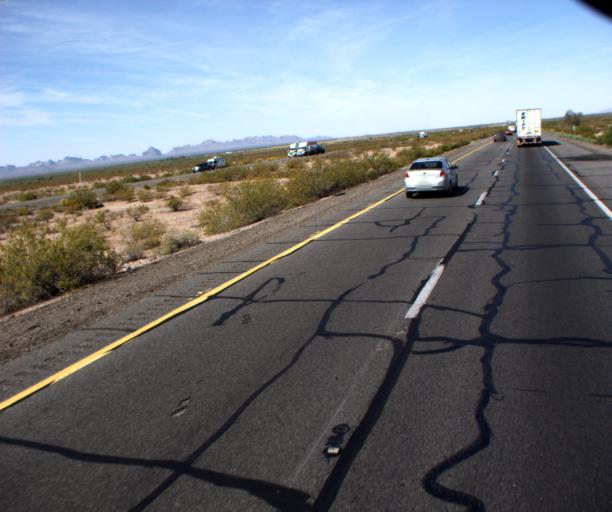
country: US
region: Arizona
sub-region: La Paz County
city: Salome
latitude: 33.5310
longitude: -113.1246
